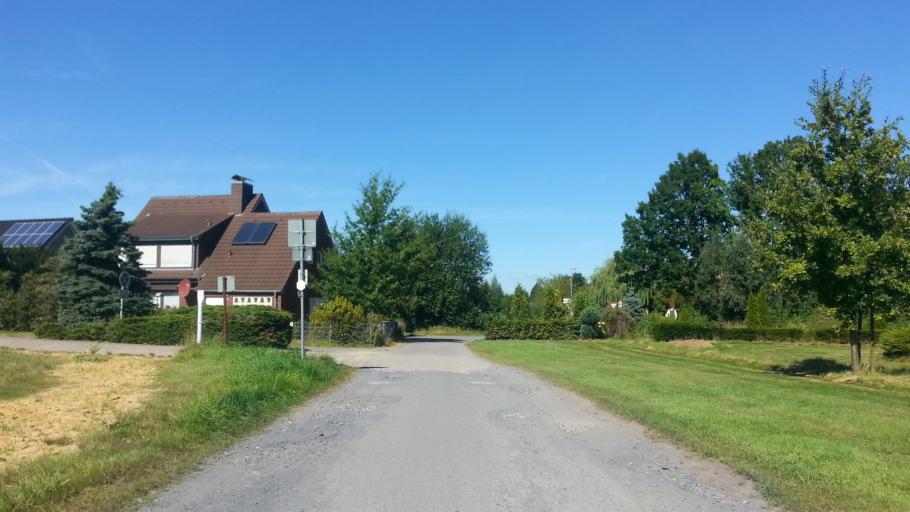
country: DE
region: North Rhine-Westphalia
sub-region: Regierungsbezirk Munster
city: Muenster
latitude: 51.9551
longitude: 7.5684
